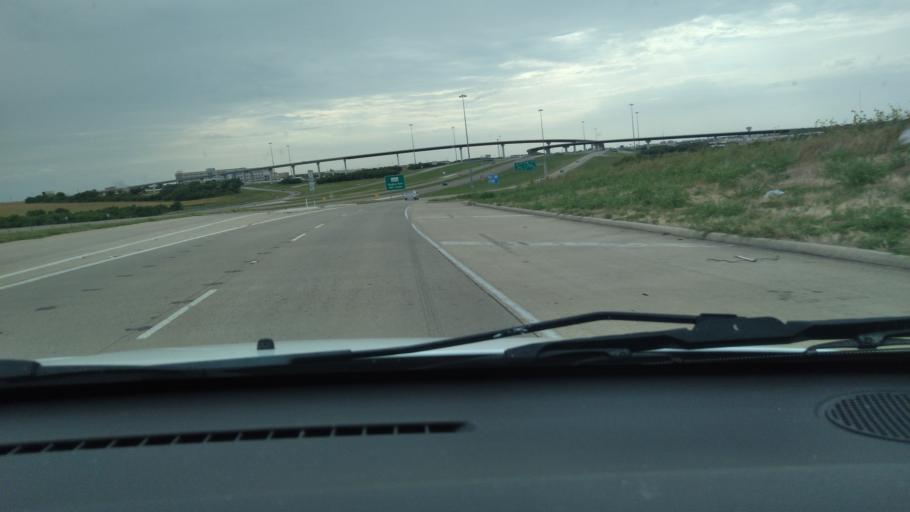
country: US
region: Texas
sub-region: McLennan County
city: Beverly Hills
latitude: 31.4912
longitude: -97.1434
